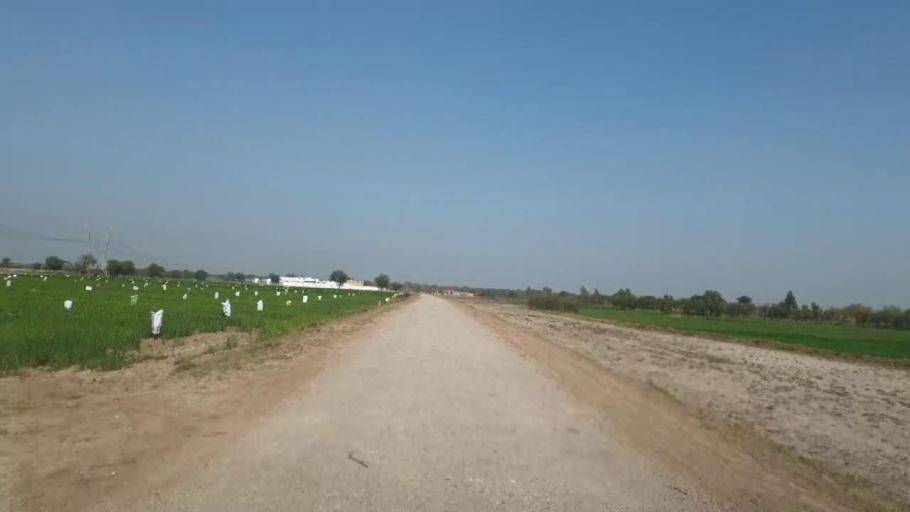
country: PK
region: Sindh
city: Matiari
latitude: 25.5031
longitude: 68.4569
